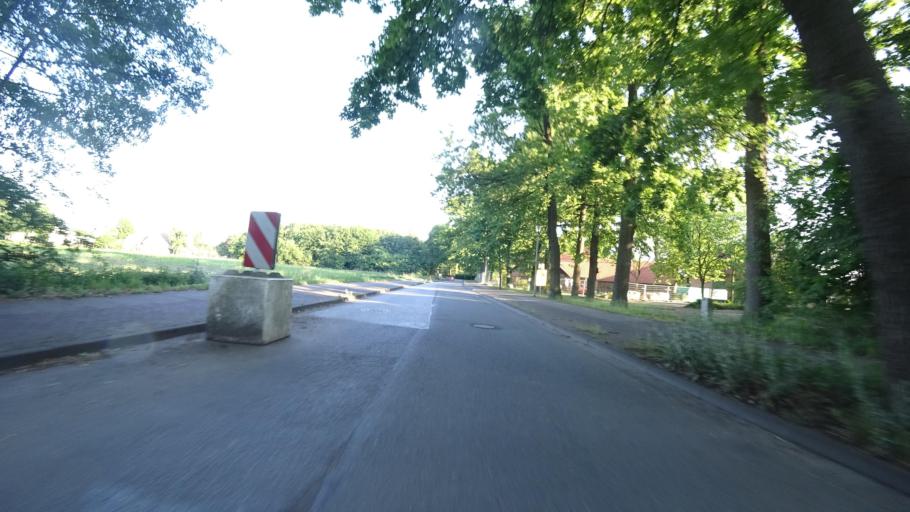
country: DE
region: North Rhine-Westphalia
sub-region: Regierungsbezirk Detmold
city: Guetersloh
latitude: 51.9235
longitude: 8.3970
